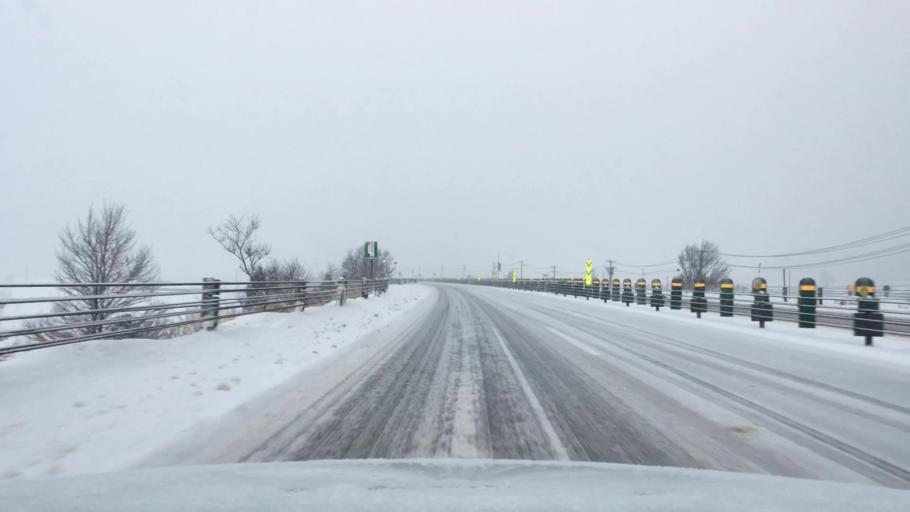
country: JP
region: Akita
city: Hanawa
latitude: 40.2910
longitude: 140.7576
